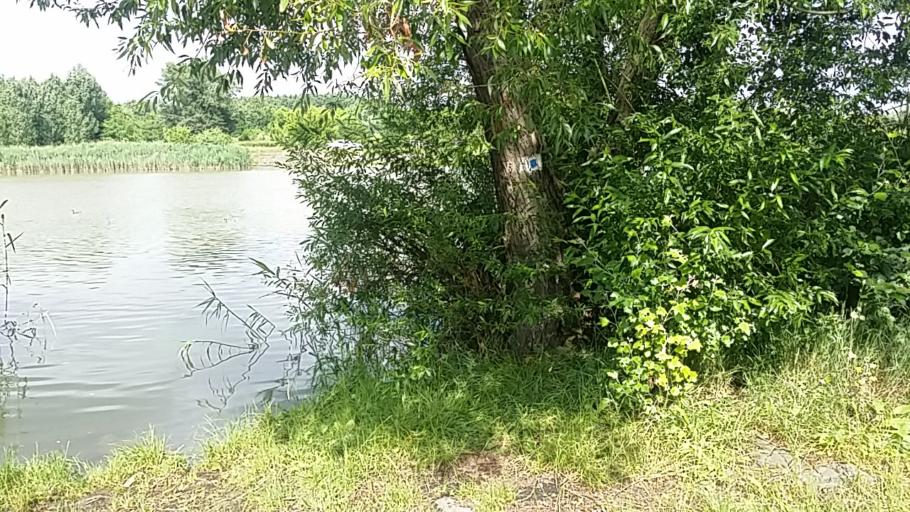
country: HU
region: Budapest
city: Budapest XX. keruelet
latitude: 47.4177
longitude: 19.0957
